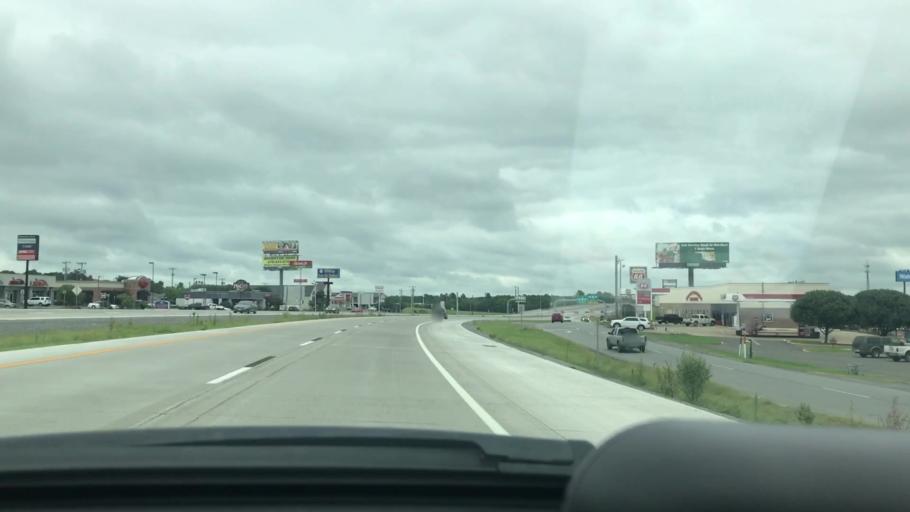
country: US
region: Oklahoma
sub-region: Pittsburg County
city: McAlester
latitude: 34.9181
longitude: -95.7451
